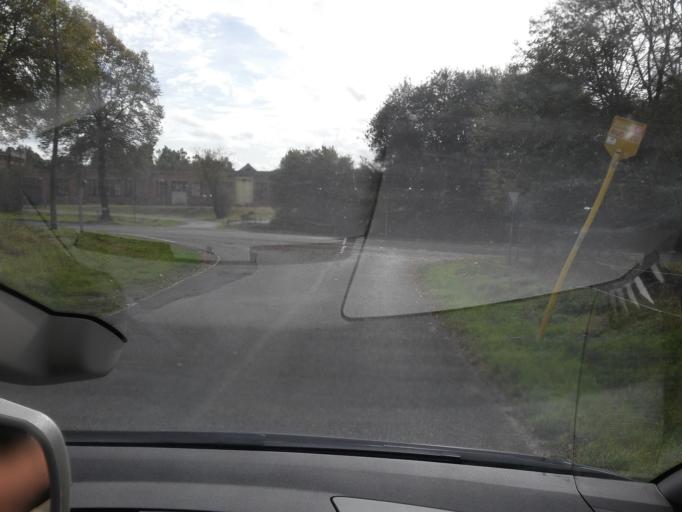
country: BE
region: Wallonia
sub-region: Province du Luxembourg
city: Arlon
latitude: 49.6912
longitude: 5.7871
